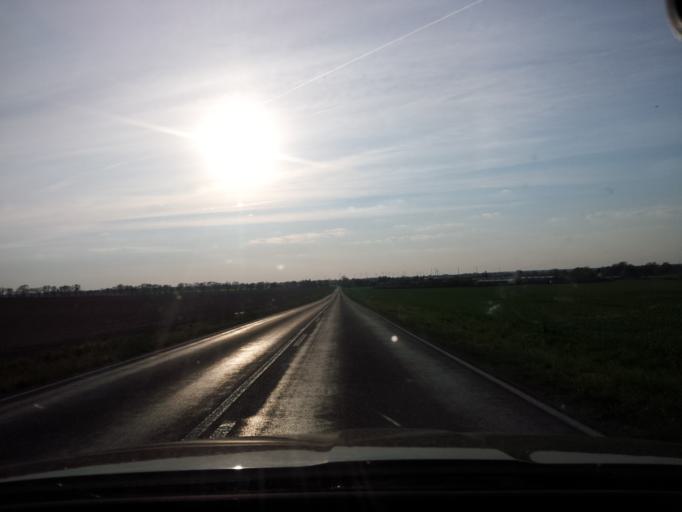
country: DE
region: Brandenburg
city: Dahme
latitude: 51.8573
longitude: 13.4770
